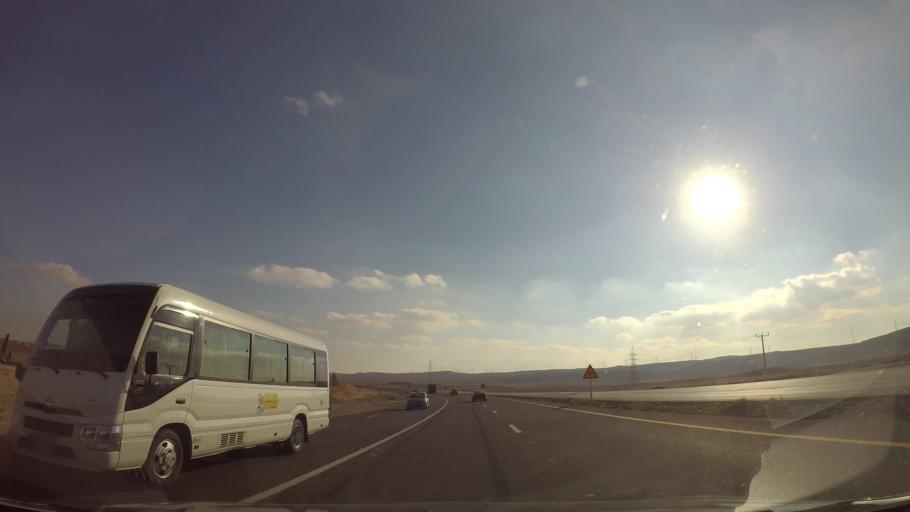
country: JO
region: Karak
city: Karak City
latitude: 31.1153
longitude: 36.0080
